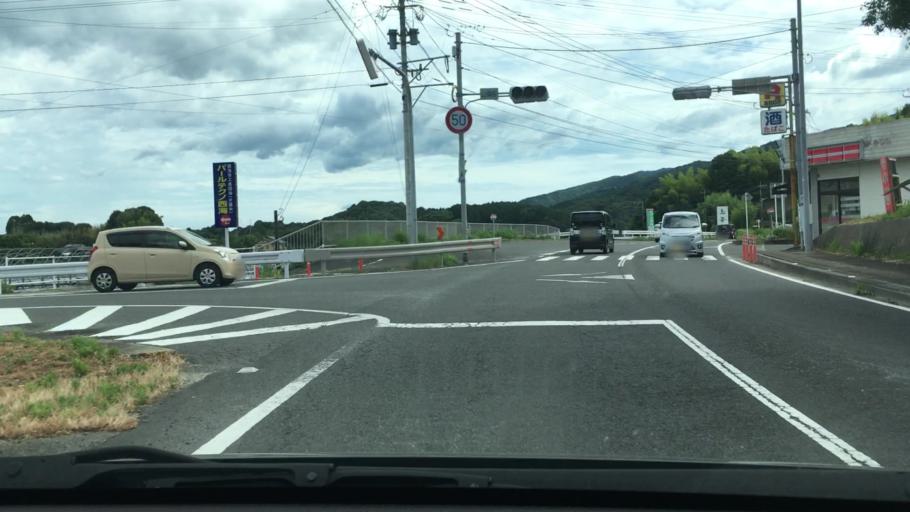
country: JP
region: Nagasaki
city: Togitsu
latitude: 32.9695
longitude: 129.7819
